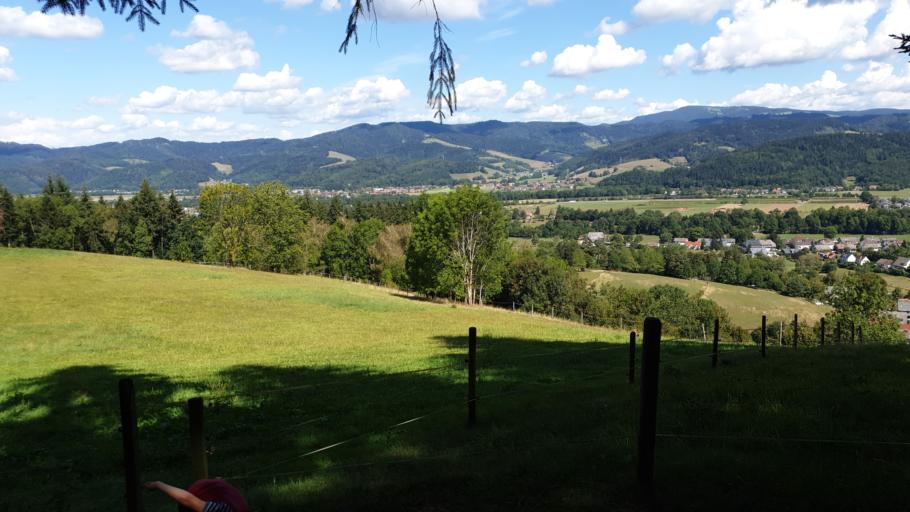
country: DE
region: Baden-Wuerttemberg
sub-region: Freiburg Region
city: Kirchzarten
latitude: 47.9535
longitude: 7.9712
